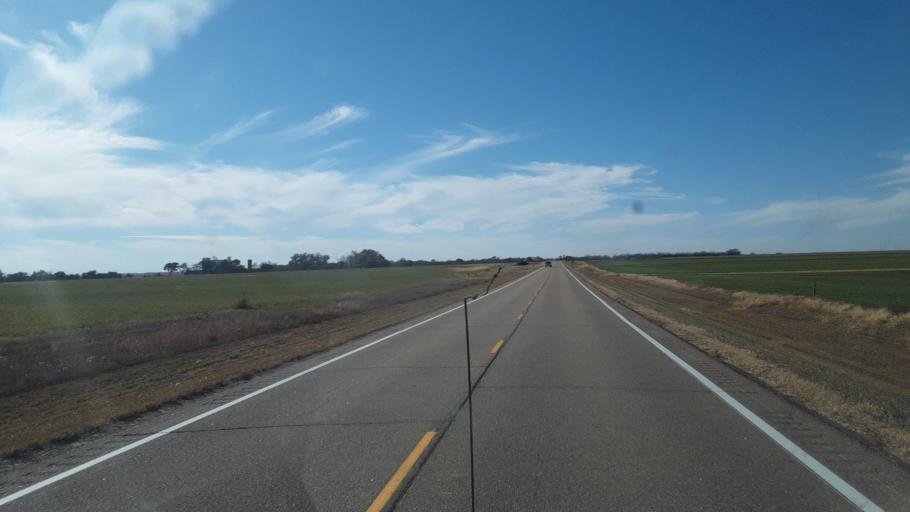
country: US
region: Kansas
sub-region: Pawnee County
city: Larned
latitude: 38.1893
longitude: -99.2872
